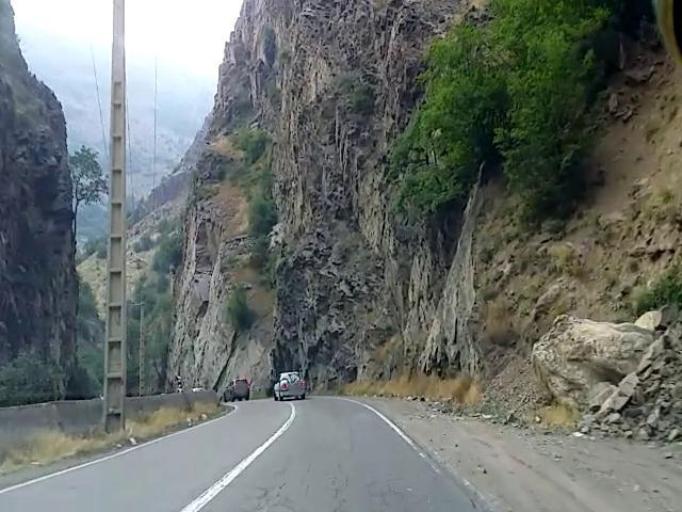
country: IR
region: Mazandaran
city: Chalus
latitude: 36.2862
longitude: 51.2430
